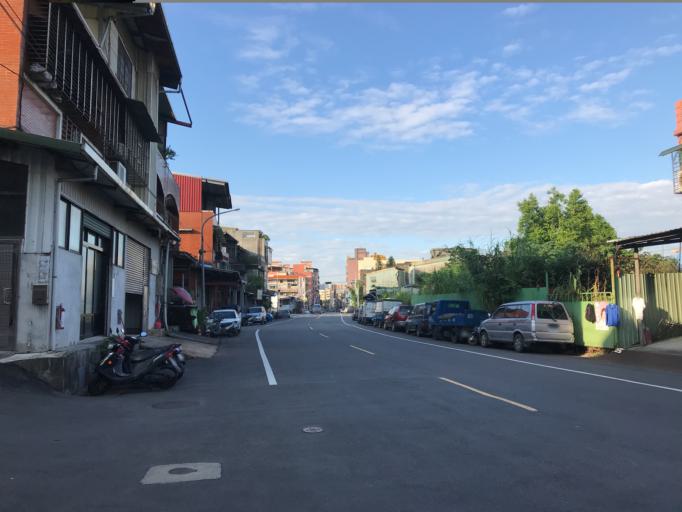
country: TW
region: Taiwan
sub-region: Taoyuan
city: Taoyuan
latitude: 24.9229
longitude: 121.3672
